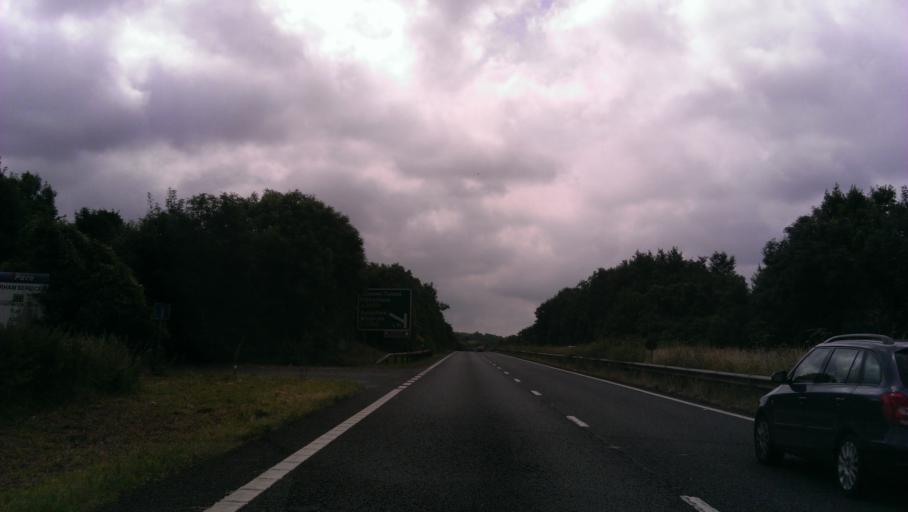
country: GB
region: England
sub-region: Kent
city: Barham
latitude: 51.2147
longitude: 1.1647
